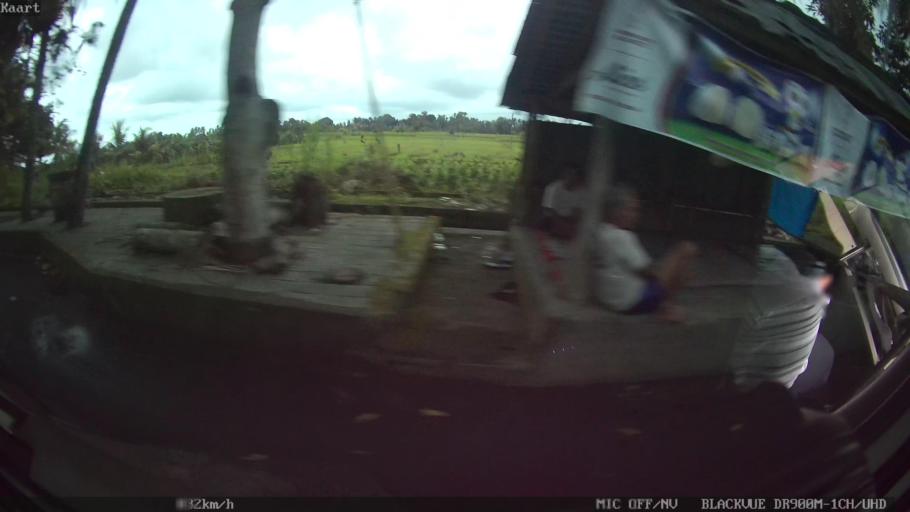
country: ID
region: Bali
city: Banjar Sempidi
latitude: -8.5254
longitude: 115.1957
